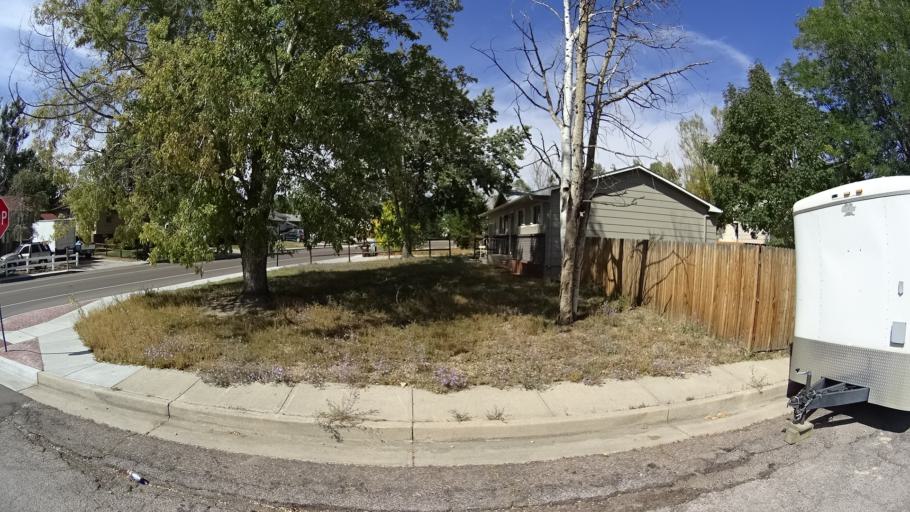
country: US
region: Colorado
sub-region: El Paso County
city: Cimarron Hills
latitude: 38.9013
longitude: -104.7541
